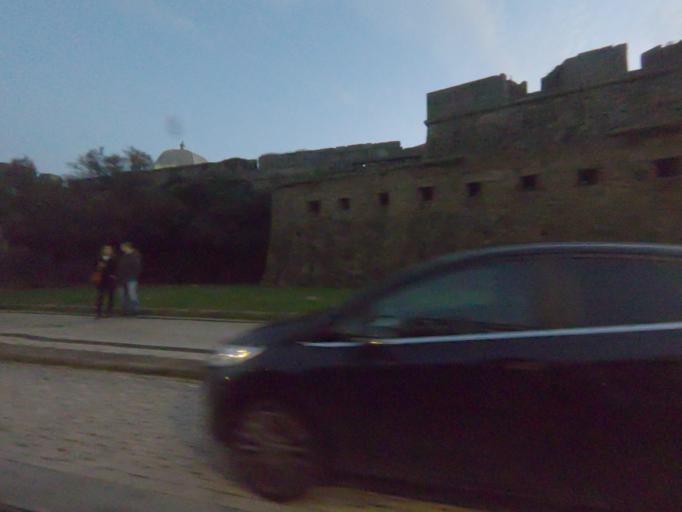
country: PT
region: Porto
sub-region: Vila Nova de Gaia
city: Canidelo
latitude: 41.1494
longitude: -8.6749
